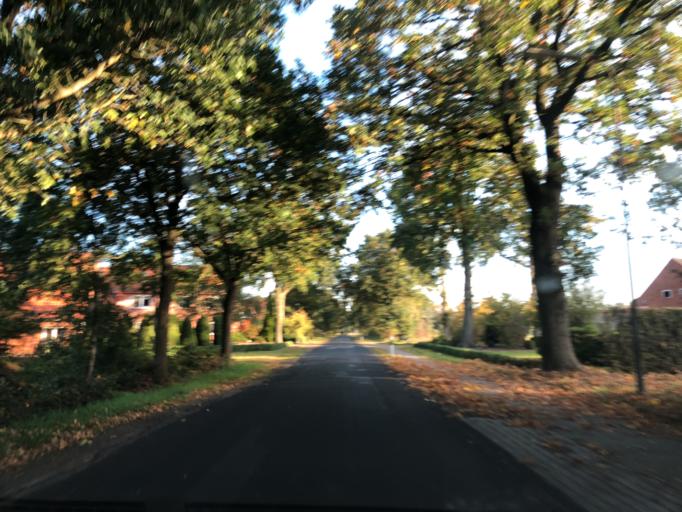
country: DE
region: Lower Saxony
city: Lehe
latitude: 53.0330
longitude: 7.3451
